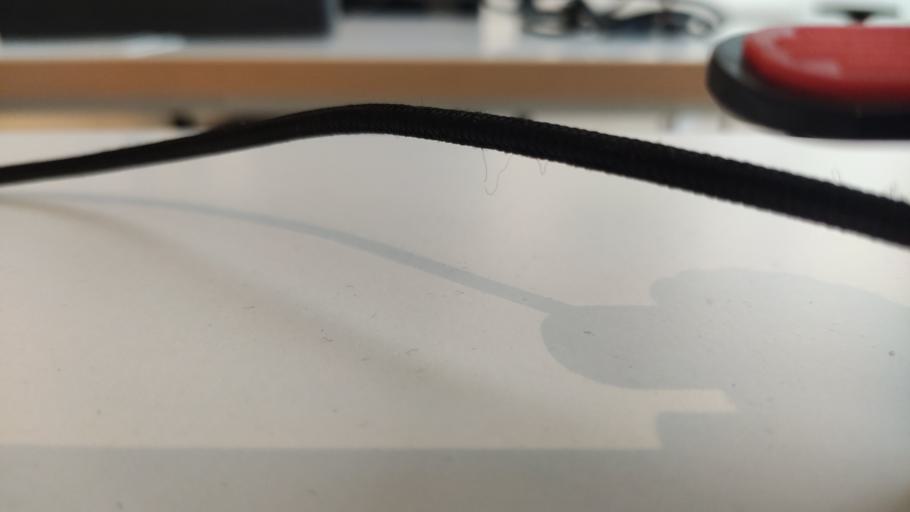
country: RU
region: Moskovskaya
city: Shevlyakovo
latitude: 56.3988
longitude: 36.8638
